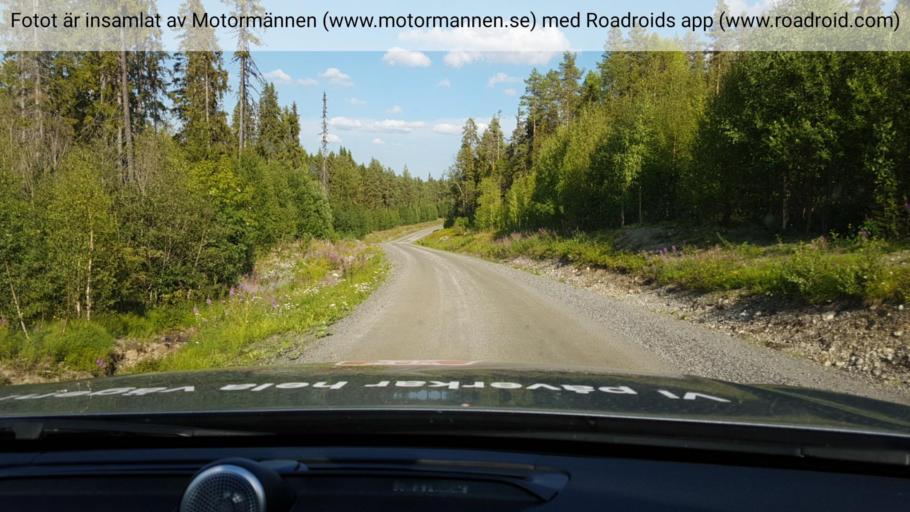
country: SE
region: Vaesterbotten
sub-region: Dorotea Kommun
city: Dorotea
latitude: 63.9214
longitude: 16.2321
